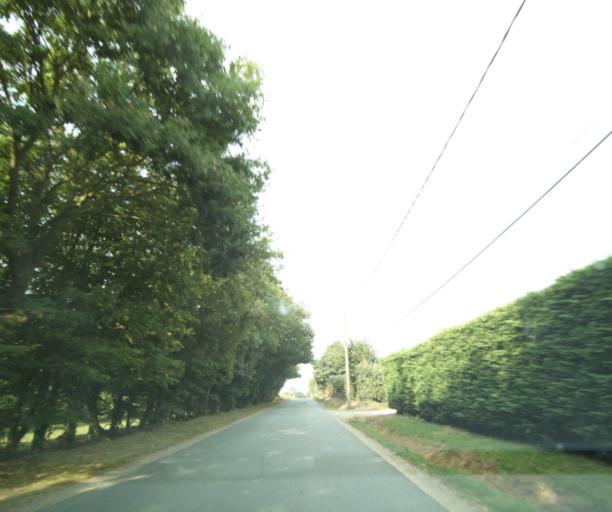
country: FR
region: Brittany
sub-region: Departement des Cotes-d'Armor
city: Jugon-les-Lacs
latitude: 48.4219
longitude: -2.3113
